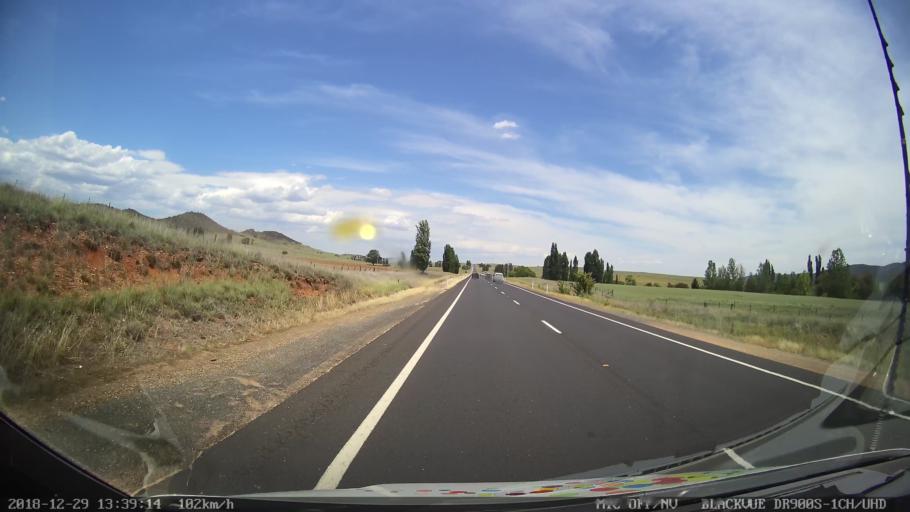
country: AU
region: New South Wales
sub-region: Cooma-Monaro
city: Cooma
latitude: -36.0102
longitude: 149.1460
